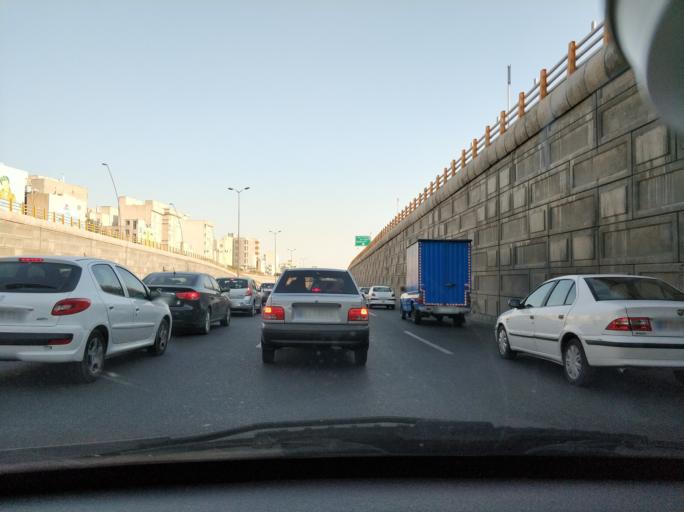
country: IR
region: Tehran
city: Tehran
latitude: 35.6938
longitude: 51.4566
